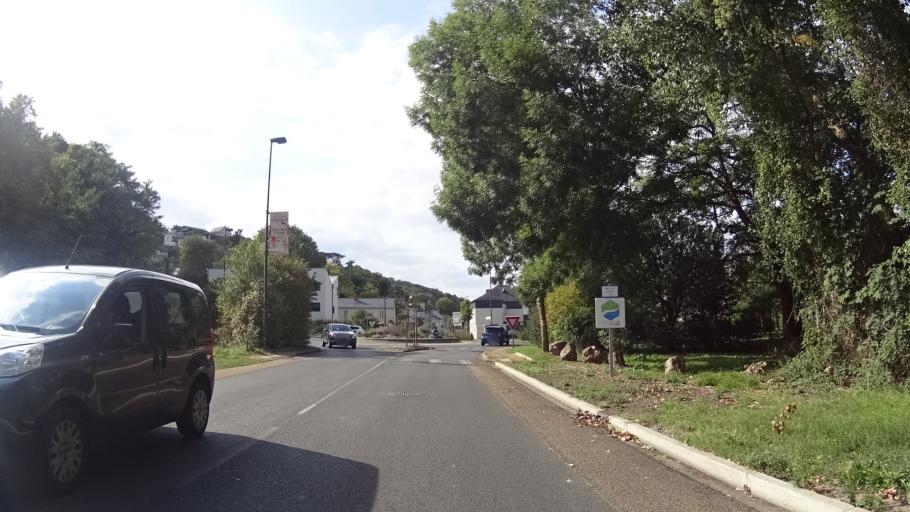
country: FR
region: Pays de la Loire
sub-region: Departement de Maine-et-Loire
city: Villebernier
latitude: 47.2499
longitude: -0.0518
